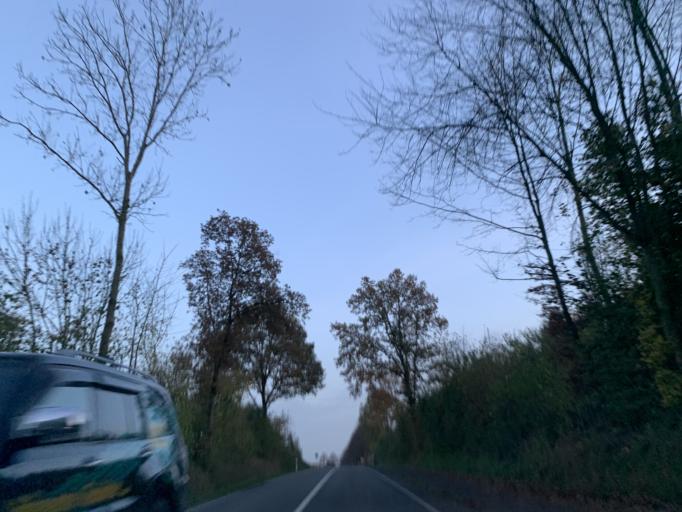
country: DE
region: North Rhine-Westphalia
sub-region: Regierungsbezirk Munster
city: Havixbeck
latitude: 51.9655
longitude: 7.4125
